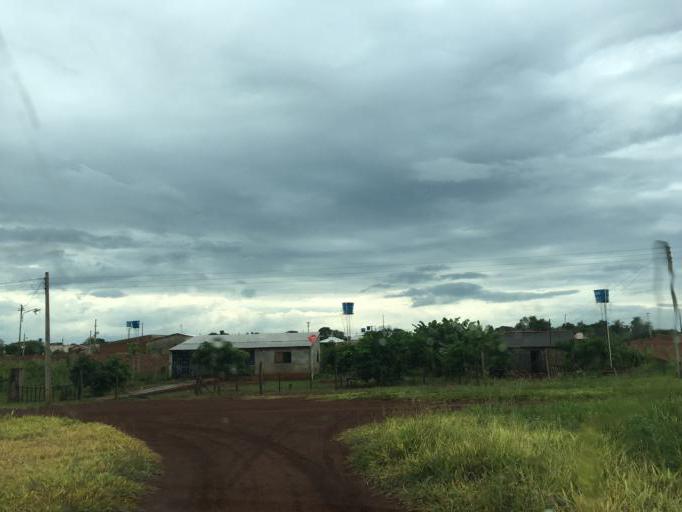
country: PY
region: Alto Parana
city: Ciudad del Este
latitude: -25.4278
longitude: -54.6535
